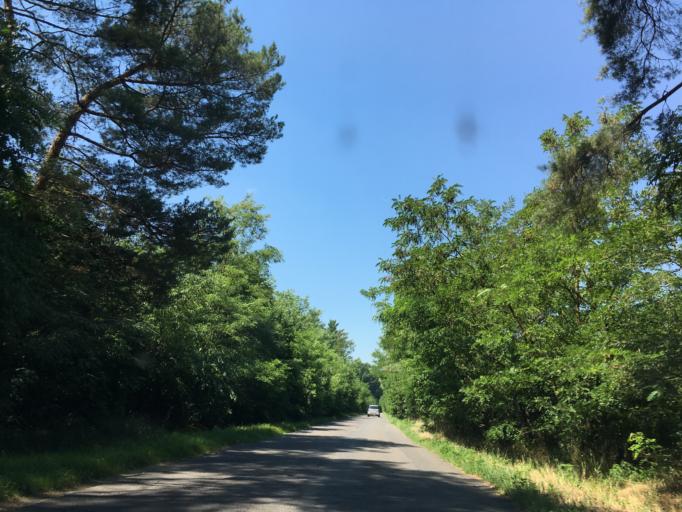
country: HU
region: Hajdu-Bihar
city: Mikepercs
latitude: 47.4682
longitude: 21.6959
